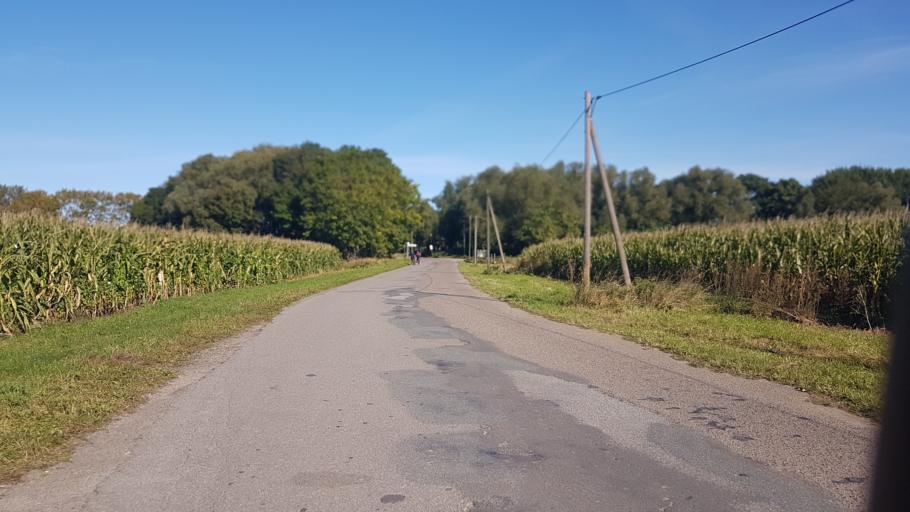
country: DE
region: Mecklenburg-Vorpommern
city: Sagard
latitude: 54.5177
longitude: 13.5305
